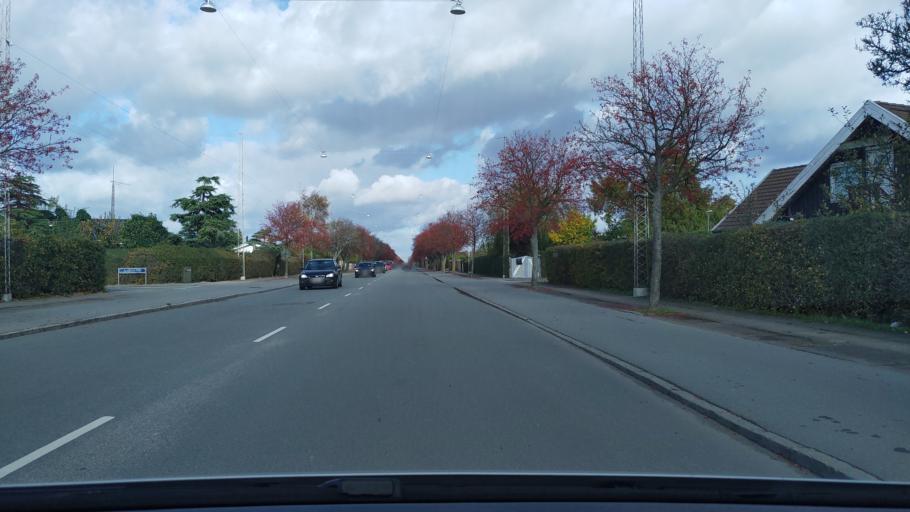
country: DK
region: Capital Region
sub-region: Tarnby Kommune
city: Tarnby
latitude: 55.5945
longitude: 12.5819
